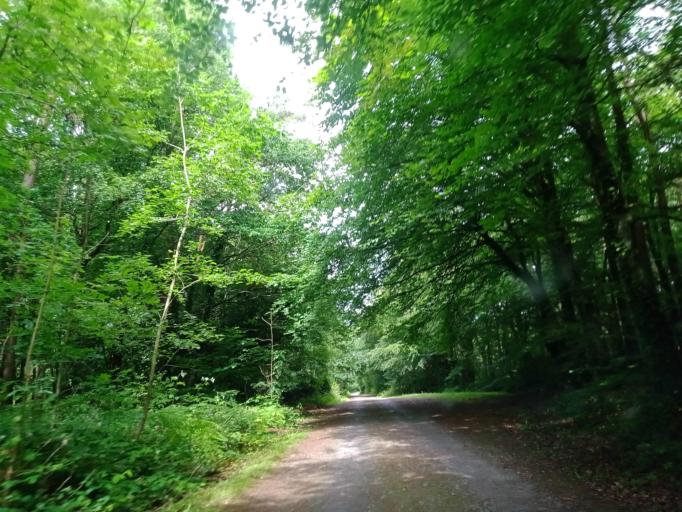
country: IE
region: Leinster
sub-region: Kilkenny
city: Thomastown
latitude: 52.5500
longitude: -7.0883
